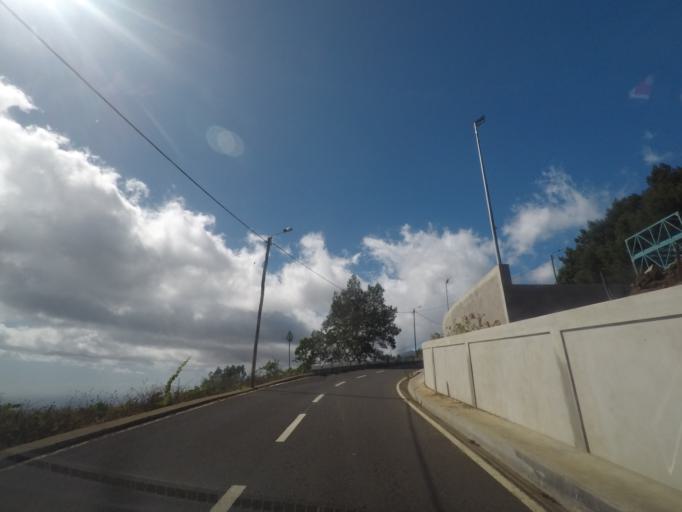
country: PT
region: Madeira
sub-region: Ribeira Brava
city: Campanario
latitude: 32.6810
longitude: -17.0403
